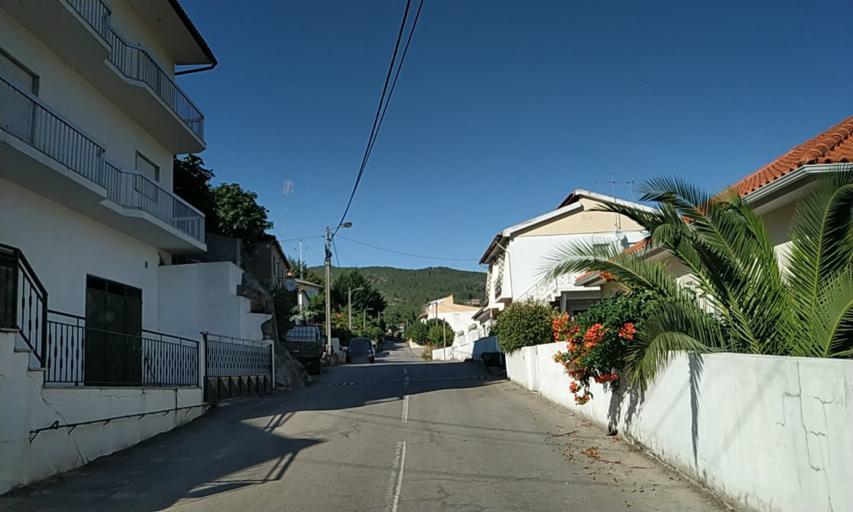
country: PT
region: Viseu
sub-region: Sao Joao da Pesqueira
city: Sao Joao da Pesqueira
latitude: 41.2516
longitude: -7.4317
